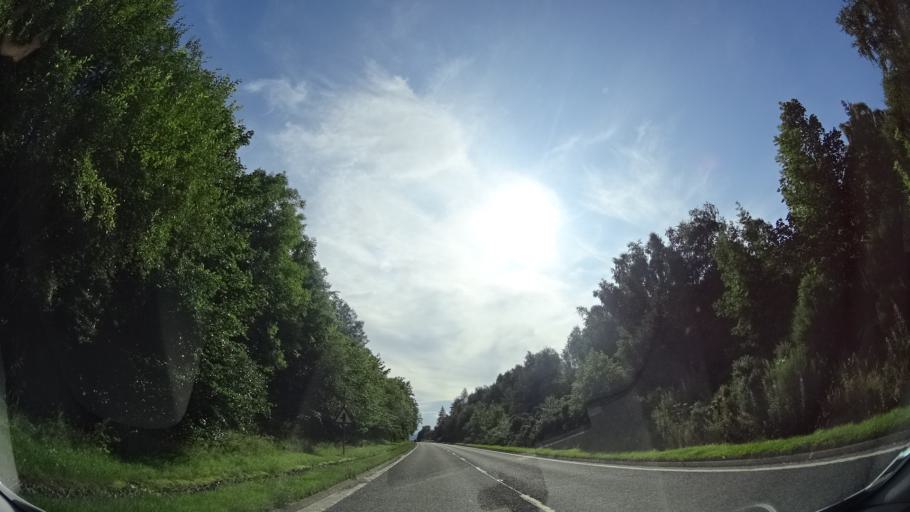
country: GB
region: Scotland
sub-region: Highland
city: Conon Bridge
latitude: 57.5649
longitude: -4.4804
